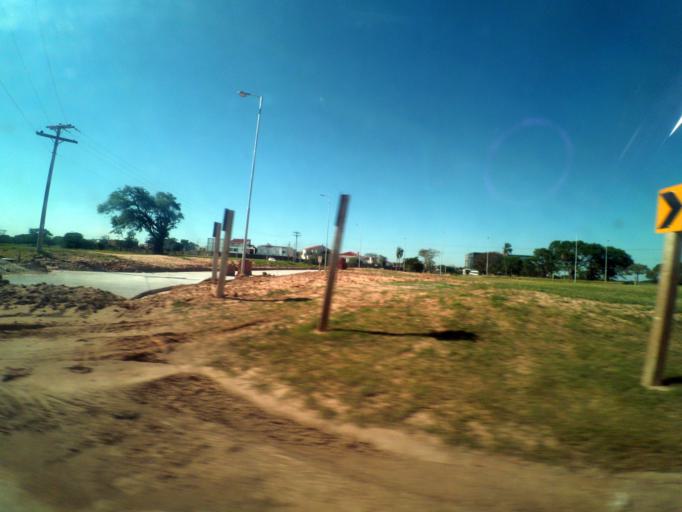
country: BO
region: Santa Cruz
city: Santa Cruz de la Sierra
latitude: -17.7552
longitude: -63.2181
